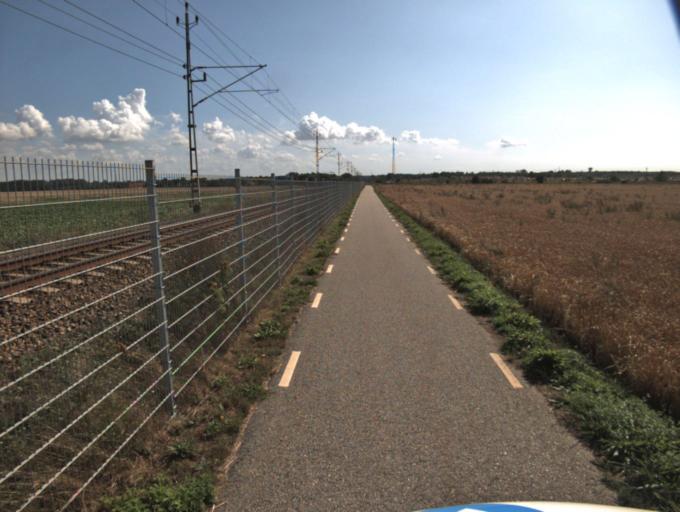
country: SE
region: Skane
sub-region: Kavlinge Kommun
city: Kaevlinge
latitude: 55.8126
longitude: 13.1094
